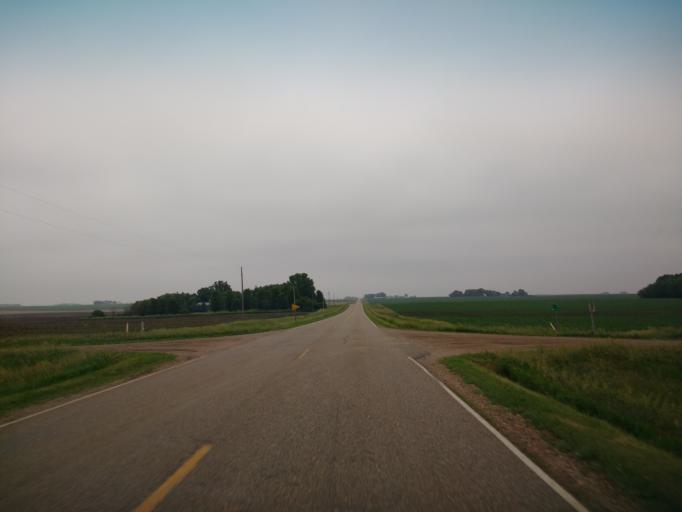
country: US
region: Iowa
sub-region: Sioux County
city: Alton
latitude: 42.9966
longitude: -95.8995
